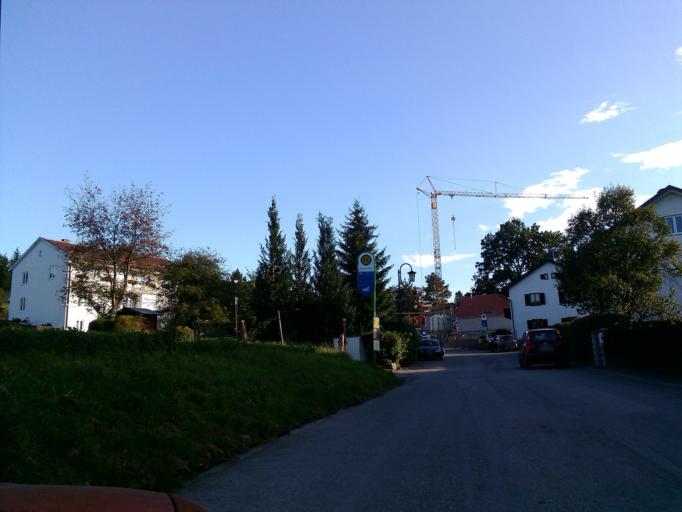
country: DE
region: Bavaria
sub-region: Upper Bavaria
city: Starnberg
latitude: 48.0267
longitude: 11.3707
